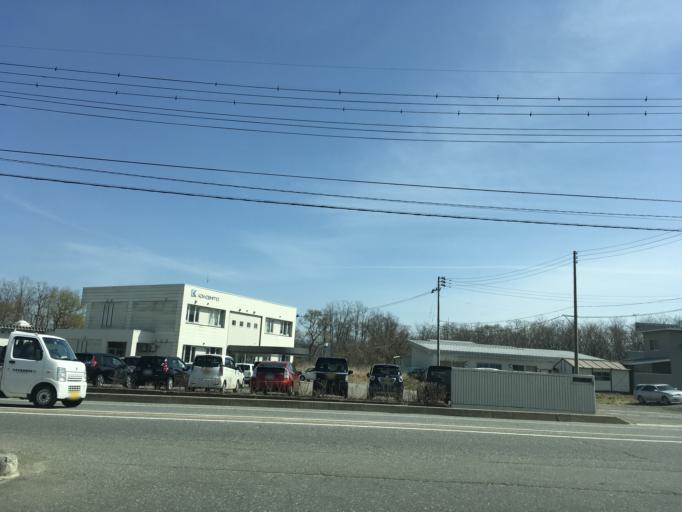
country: JP
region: Yamagata
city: Yonezawa
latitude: 37.9108
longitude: 140.1346
